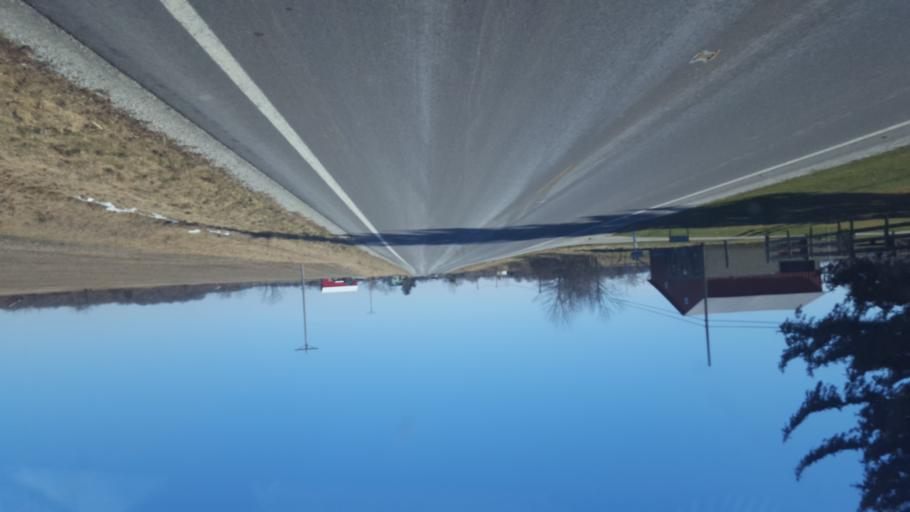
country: US
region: Ohio
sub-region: Hardin County
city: Kenton
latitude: 40.6433
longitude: -83.4664
